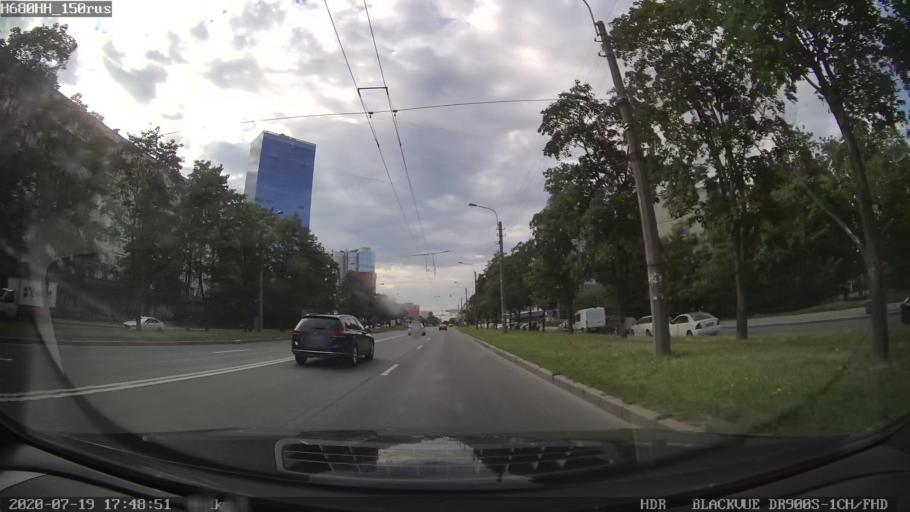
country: RU
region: St.-Petersburg
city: Kupchino
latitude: 59.8493
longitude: 30.3099
